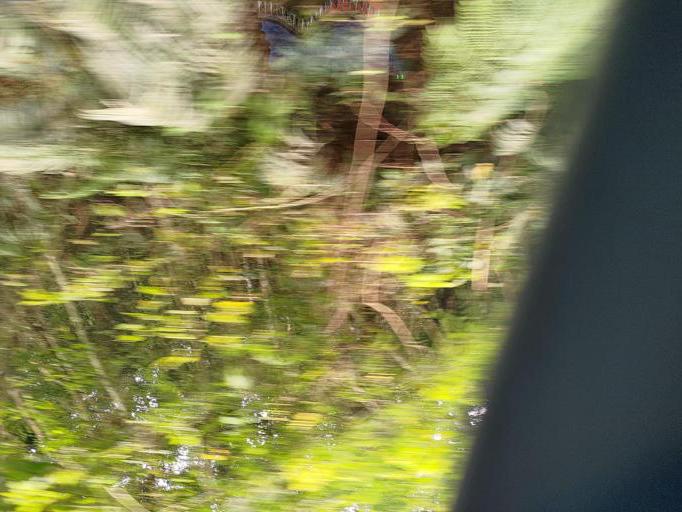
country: TW
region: Taiwan
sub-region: Hsinchu
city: Hsinchu
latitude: 24.6225
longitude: 121.0502
